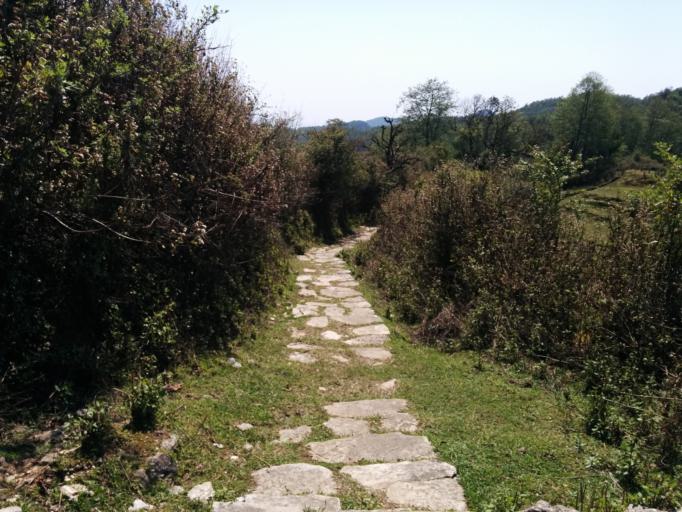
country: NP
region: Western Region
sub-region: Gandaki Zone
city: Pokhara
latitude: 28.2204
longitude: 83.8087
